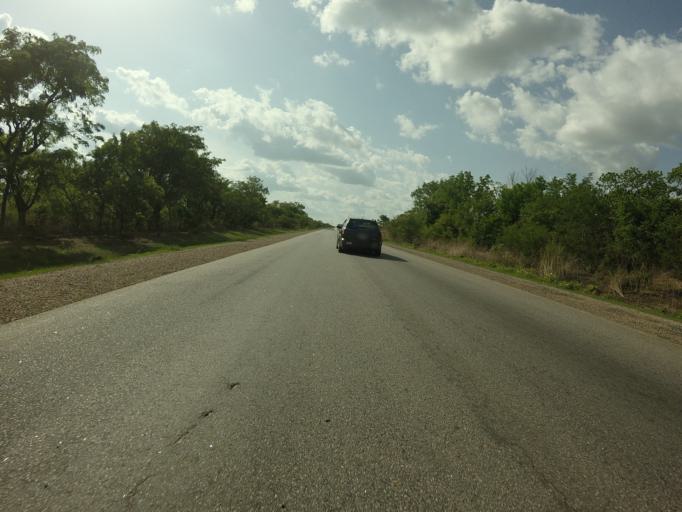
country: GH
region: Upper East
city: Bolgatanga
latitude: 10.5292
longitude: -0.8173
